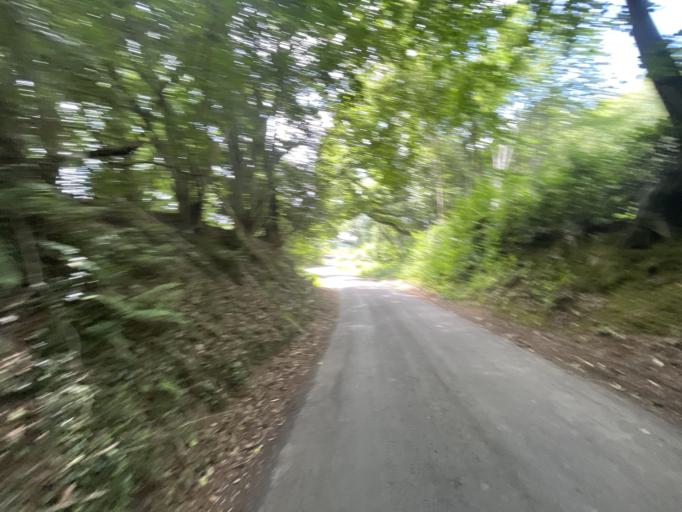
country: GB
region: England
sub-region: Kent
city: Edenbridge
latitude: 51.1650
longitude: 0.1301
